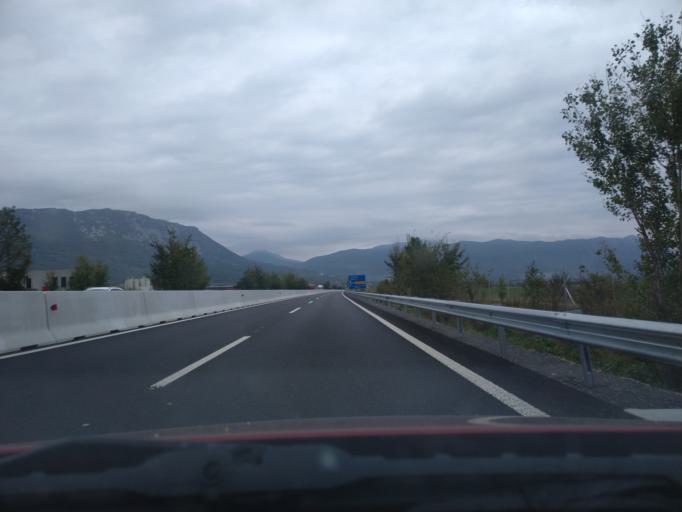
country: SI
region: Ajdovscina
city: Lokavec
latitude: 45.8837
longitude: 13.8855
